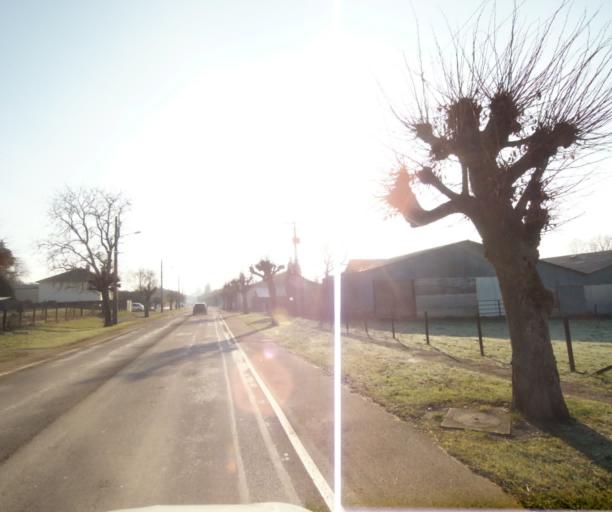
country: FR
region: Champagne-Ardenne
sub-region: Departement de la Haute-Marne
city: Montier-en-Der
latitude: 48.4833
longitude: 4.7632
